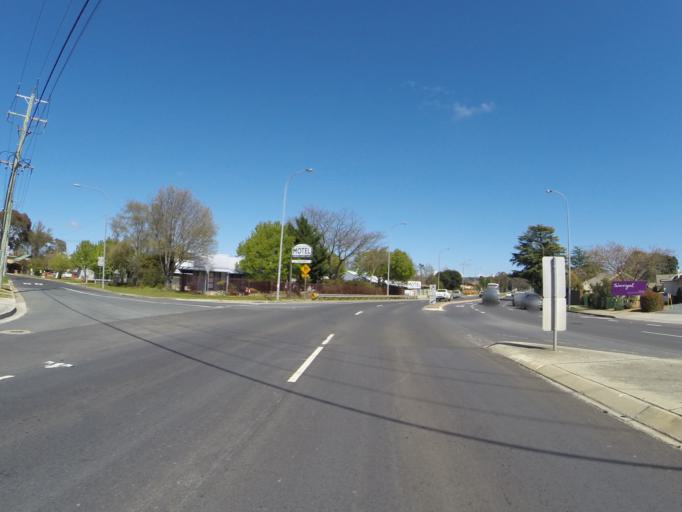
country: AU
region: New South Wales
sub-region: Queanbeyan
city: Queanbeyan
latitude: -35.3561
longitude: 149.2288
